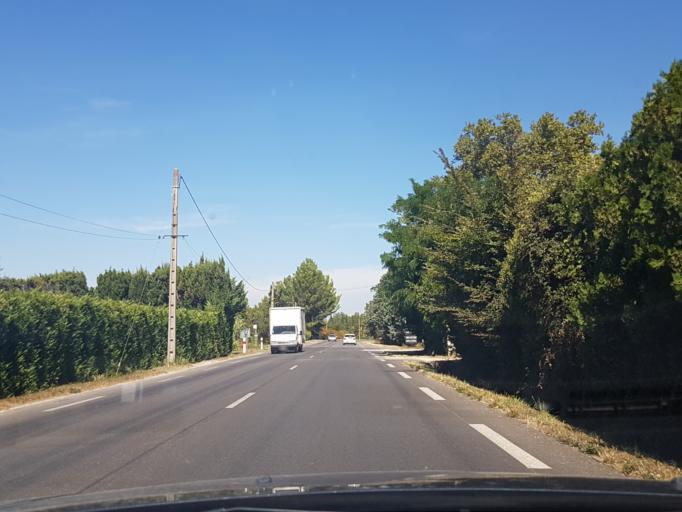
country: FR
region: Provence-Alpes-Cote d'Azur
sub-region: Departement des Bouches-du-Rhone
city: Saint-Remy-de-Provence
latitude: 43.8093
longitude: 4.8336
